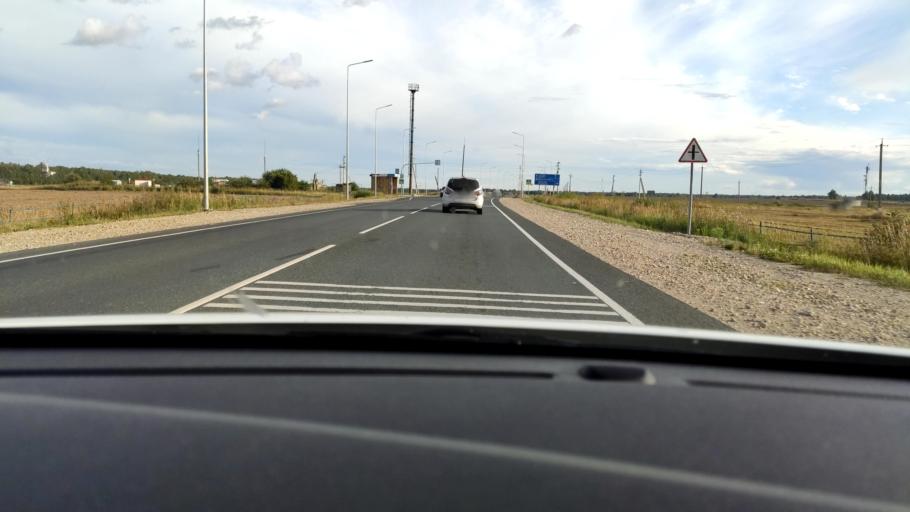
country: RU
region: Mariy-El
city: Suslonger
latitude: 56.2167
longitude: 48.2367
